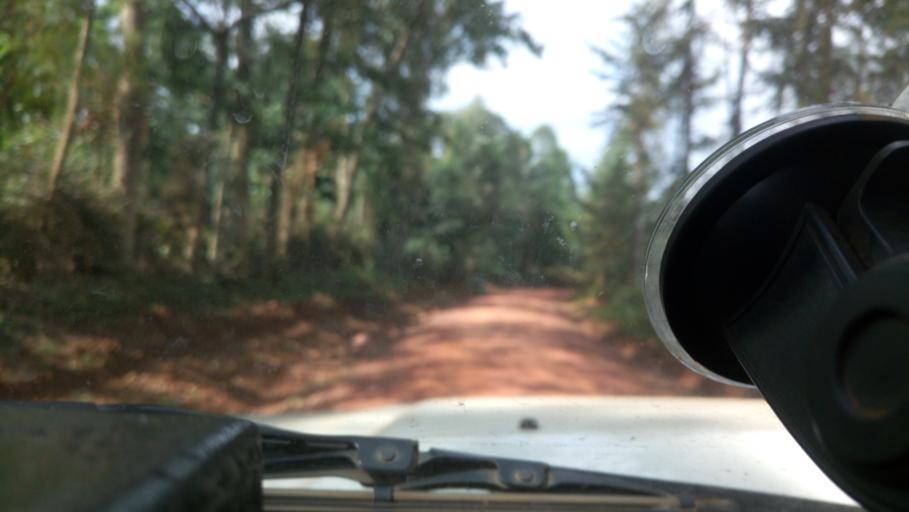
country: KE
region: Nyamira District
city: Nyamira
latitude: -0.5685
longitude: 35.0624
